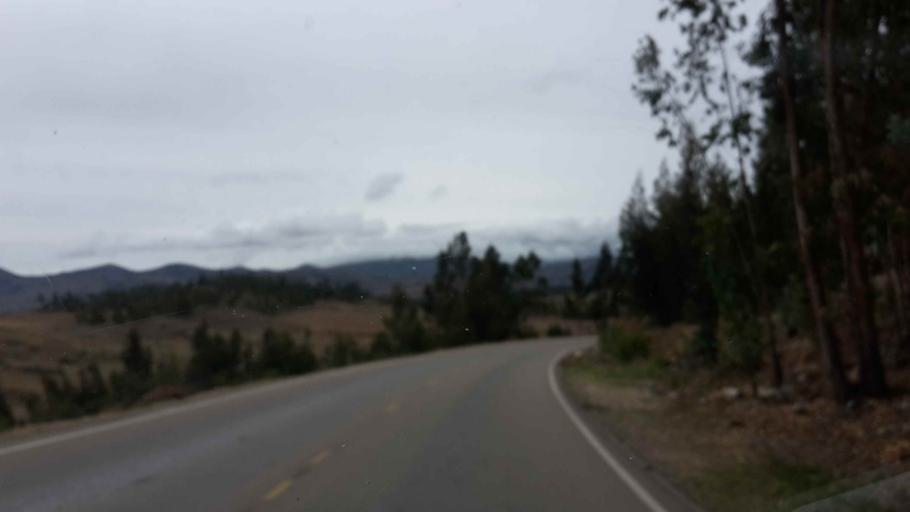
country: BO
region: Cochabamba
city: Arani
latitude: -17.4602
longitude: -65.7073
